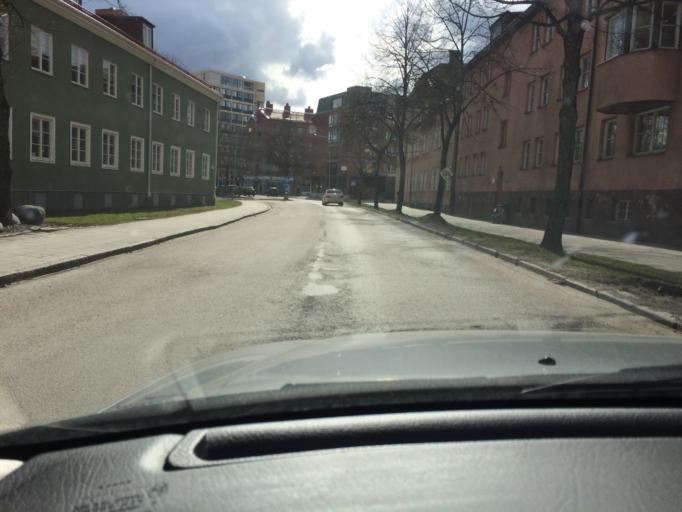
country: SE
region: Vaestmanland
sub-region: Vasteras
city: Vasteras
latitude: 59.6135
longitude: 16.5490
